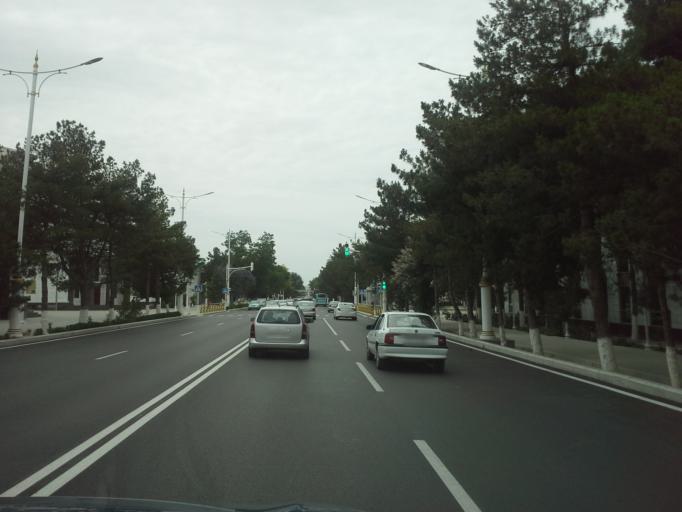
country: TM
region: Ahal
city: Ashgabat
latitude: 37.9453
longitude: 58.3822
